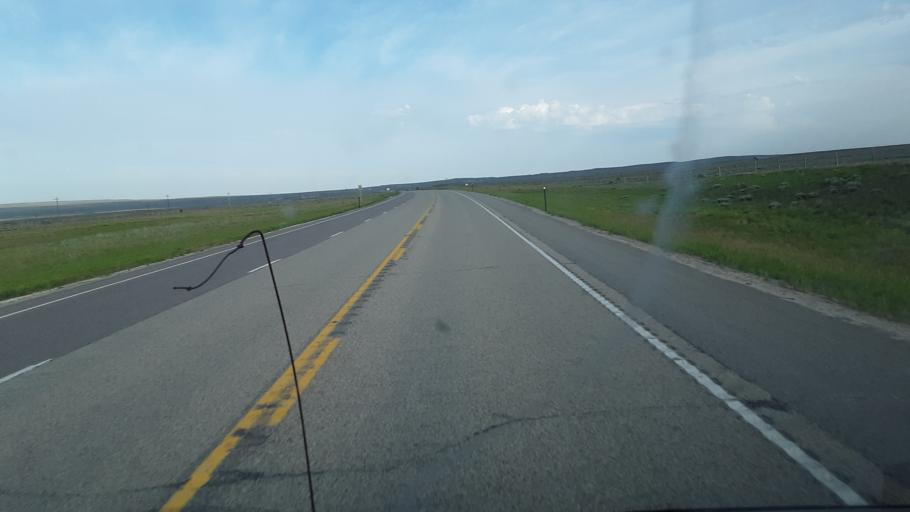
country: US
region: Wyoming
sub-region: Natrona County
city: Mills
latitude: 43.0659
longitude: -107.1660
